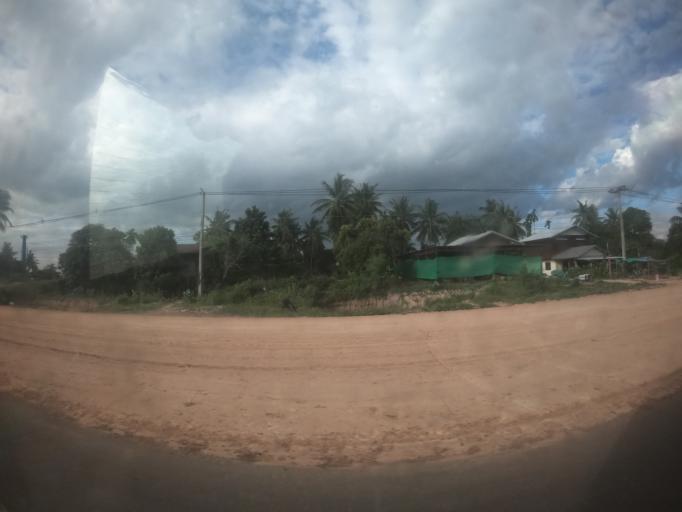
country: TH
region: Surin
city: Kap Choeng
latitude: 14.4911
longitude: 103.5737
